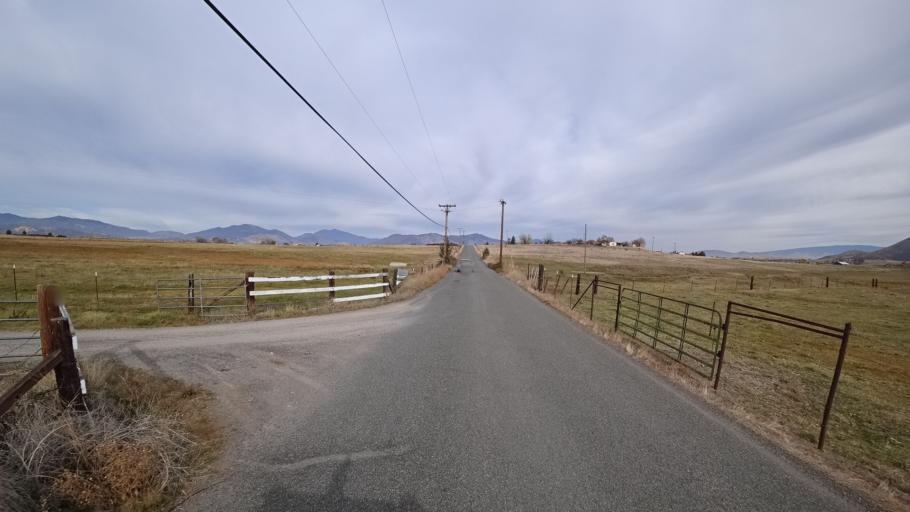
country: US
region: California
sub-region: Siskiyou County
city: Montague
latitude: 41.7002
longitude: -122.5496
